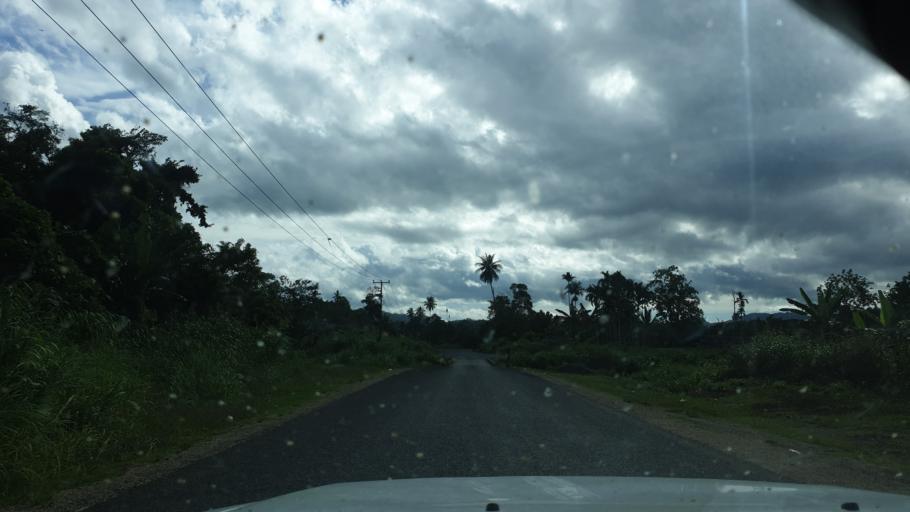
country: PG
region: Madang
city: Madang
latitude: -5.1075
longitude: 145.7924
